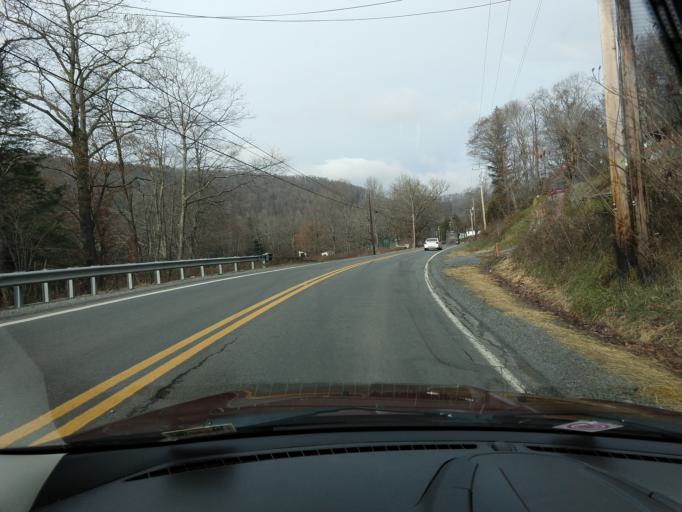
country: US
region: West Virginia
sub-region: Greenbrier County
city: Rainelle
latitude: 37.9879
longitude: -80.7286
